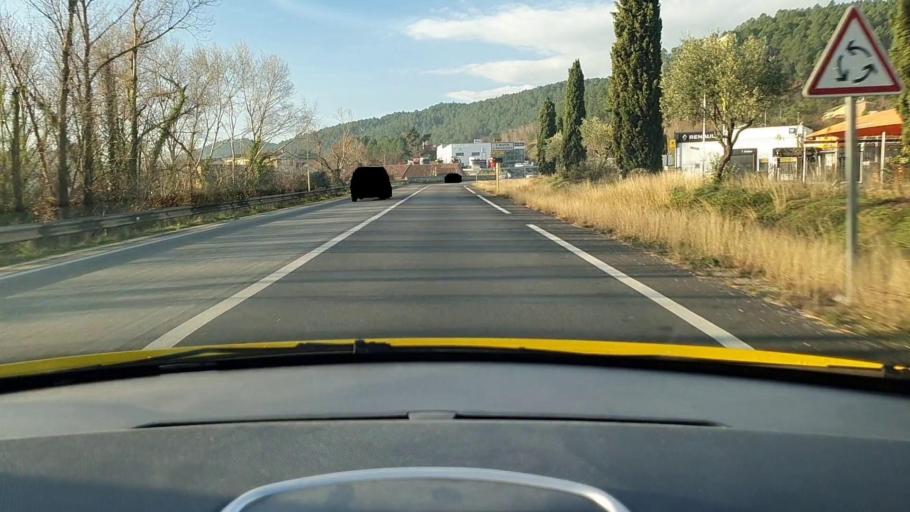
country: FR
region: Languedoc-Roussillon
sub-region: Departement du Gard
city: Saint-Martin-de-Valgalgues
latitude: 44.1577
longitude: 4.0860
